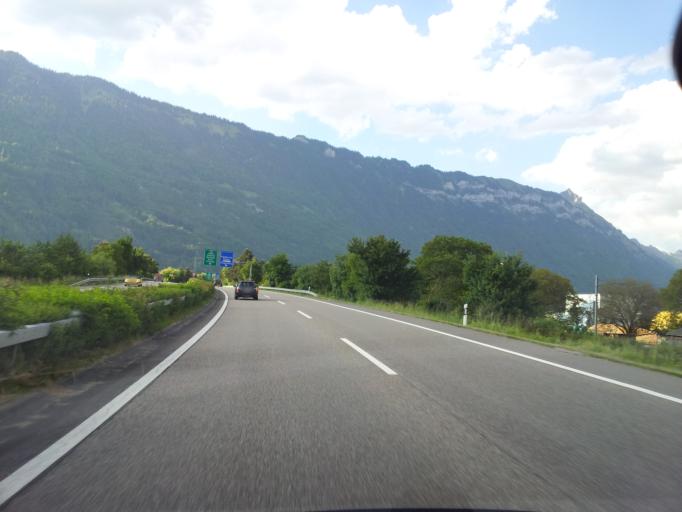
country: CH
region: Bern
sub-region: Interlaken-Oberhasli District
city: Matten
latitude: 46.6783
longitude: 7.8760
